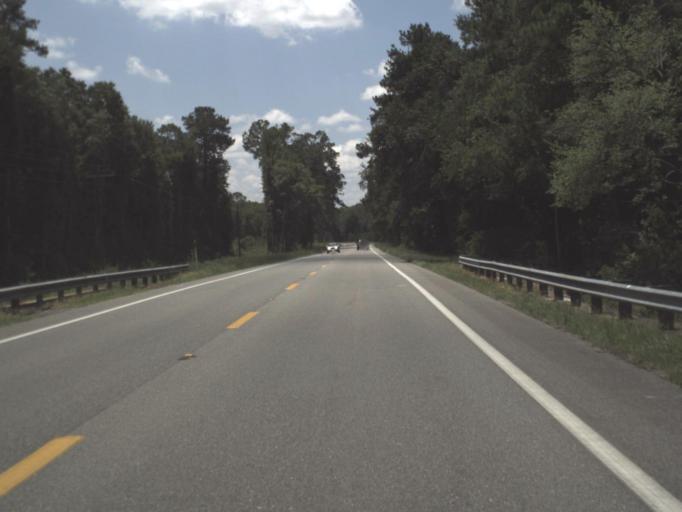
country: US
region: Florida
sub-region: Madison County
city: Madison
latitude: 30.5084
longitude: -83.6329
